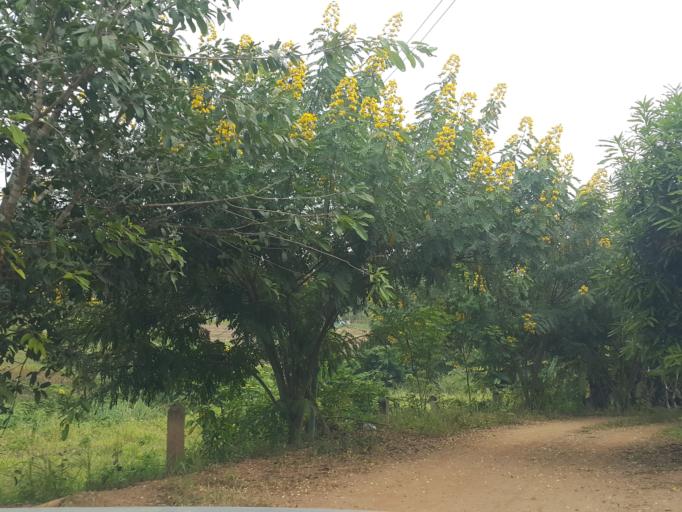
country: TH
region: Mae Hong Son
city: Wiang Nuea
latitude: 19.3833
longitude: 98.4625
